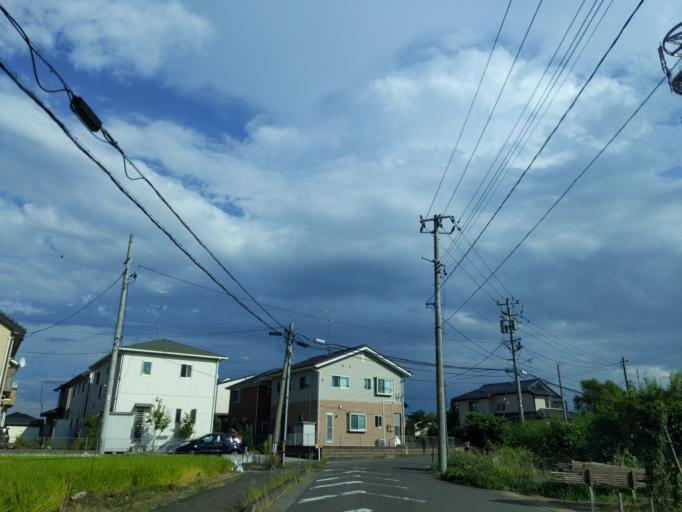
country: JP
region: Fukushima
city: Koriyama
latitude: 37.3824
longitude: 140.3276
